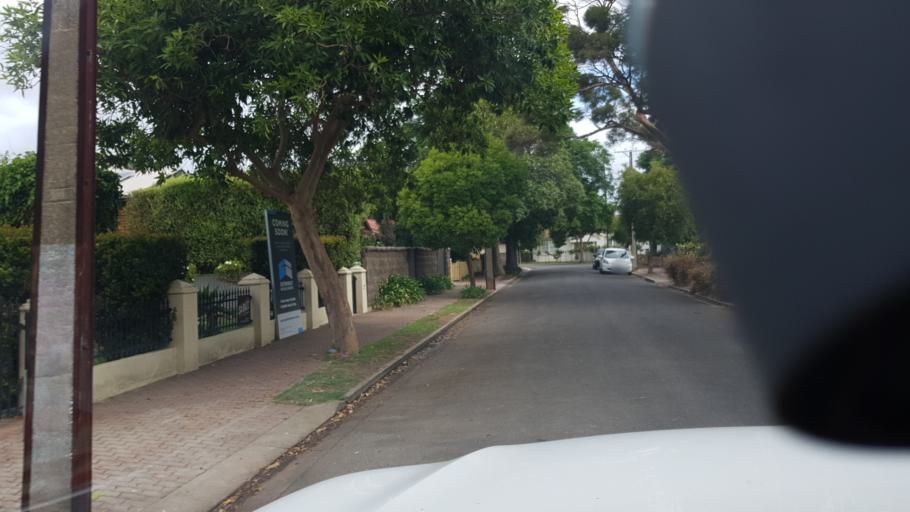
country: AU
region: South Australia
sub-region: Holdfast Bay
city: Glenelg East
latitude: -34.9701
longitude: 138.5230
